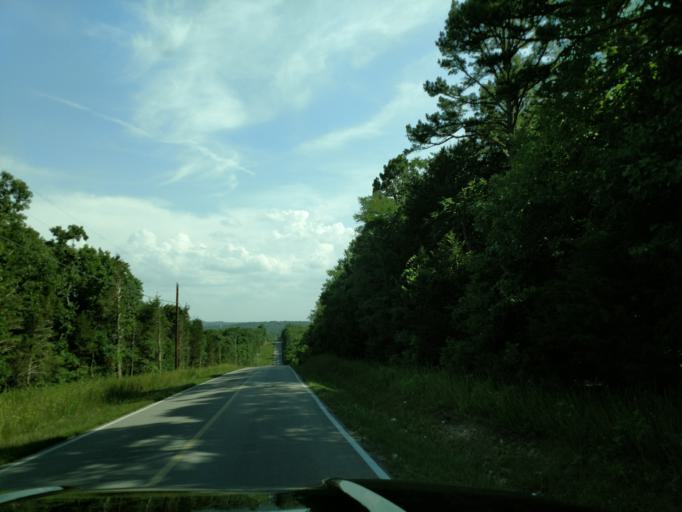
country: US
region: Missouri
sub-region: Barry County
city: Shell Knob
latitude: 36.6089
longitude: -93.5811
